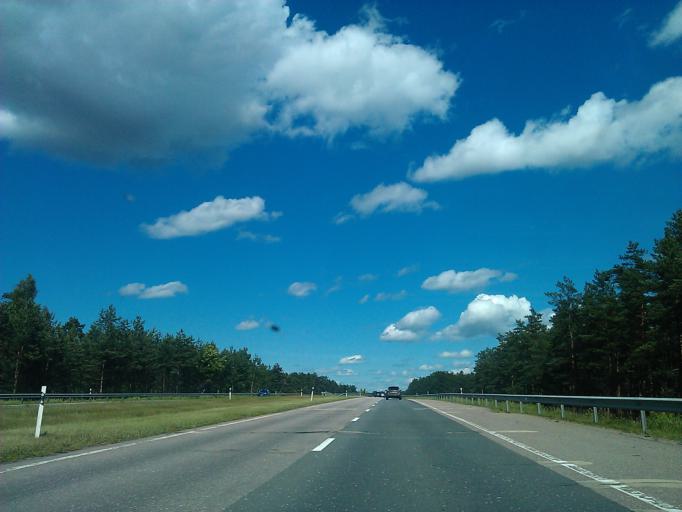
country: LV
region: Garkalne
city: Garkalne
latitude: 57.0523
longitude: 24.4488
